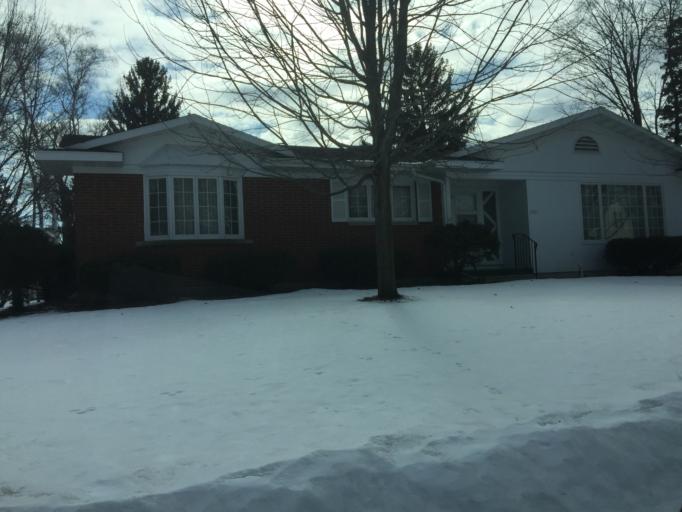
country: US
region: Wisconsin
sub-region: Oconto County
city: Oconto
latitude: 44.8900
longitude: -87.8736
